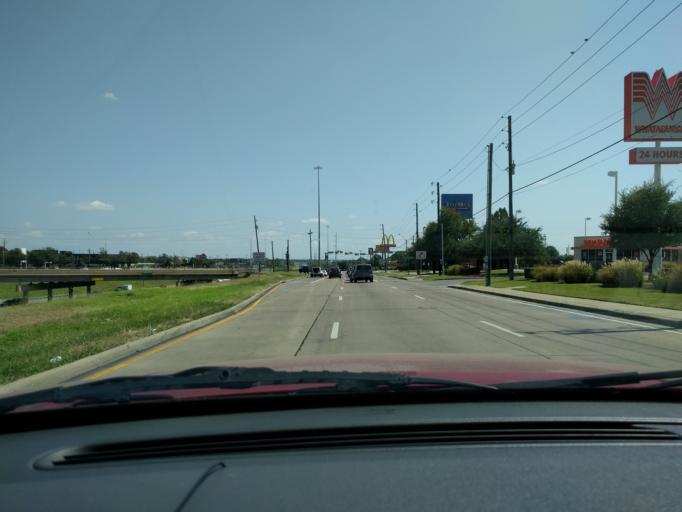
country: US
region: Texas
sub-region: Dallas County
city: Richardson
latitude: 32.9116
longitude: -96.7367
